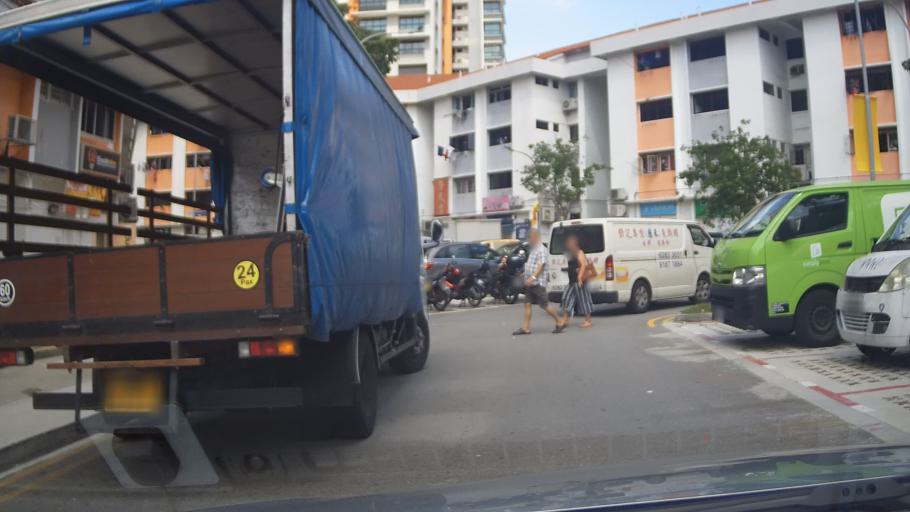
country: SG
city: Singapore
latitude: 1.3140
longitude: 103.7640
